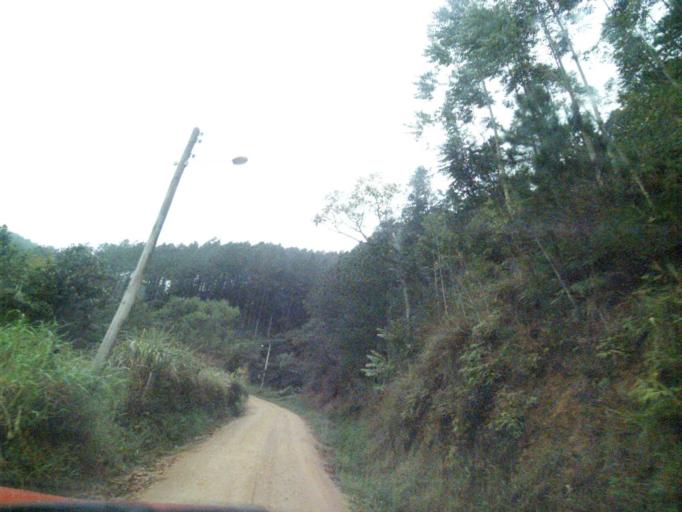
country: BR
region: Santa Catarina
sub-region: Anitapolis
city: Anitapolis
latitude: -27.9085
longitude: -49.1217
